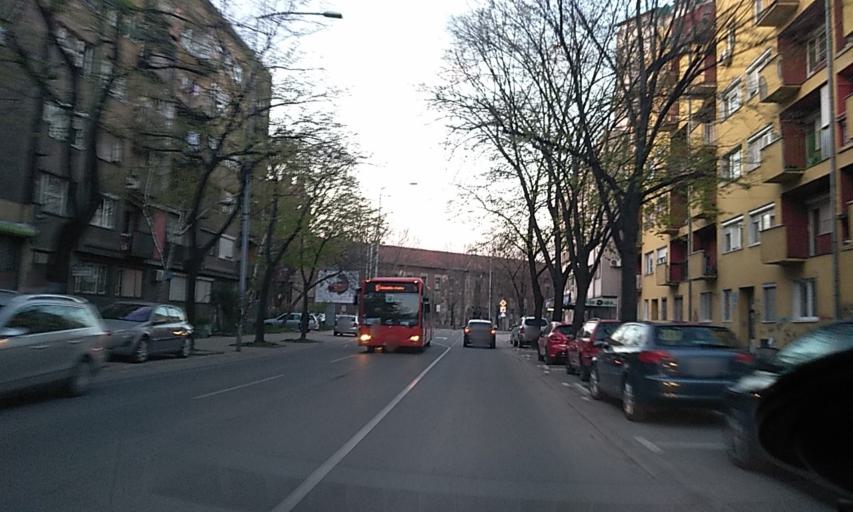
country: RS
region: Central Serbia
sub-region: Nisavski Okrug
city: Nis
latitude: 43.3188
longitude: 21.8873
